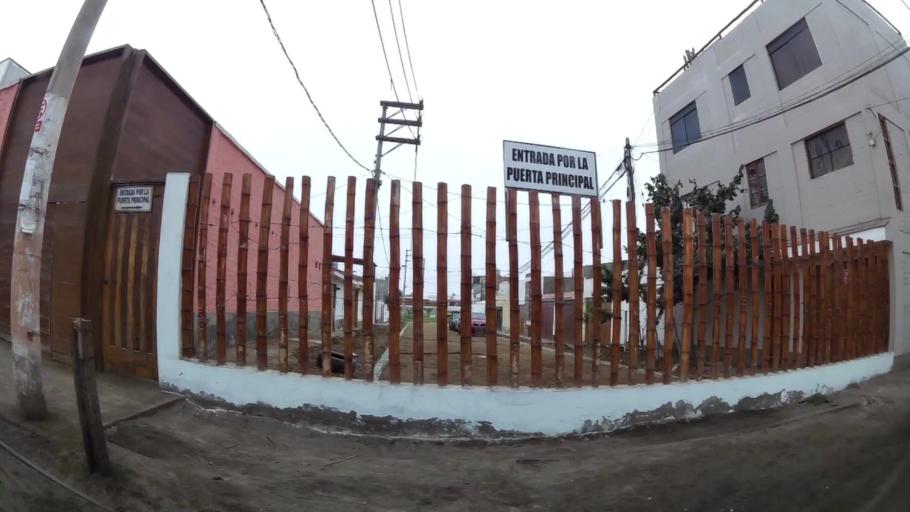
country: PE
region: Lima
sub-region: Lima
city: Punta Hermosa
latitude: -12.3328
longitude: -76.8291
